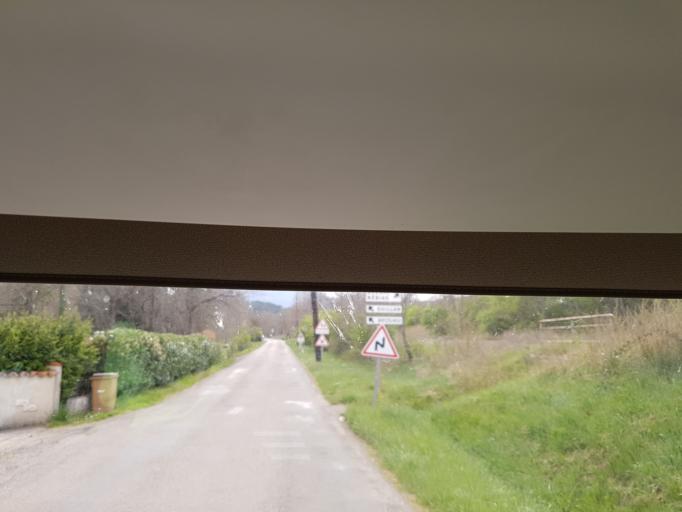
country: FR
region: Languedoc-Roussillon
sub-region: Departement de l'Aude
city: Quillan
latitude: 42.9081
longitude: 2.1909
